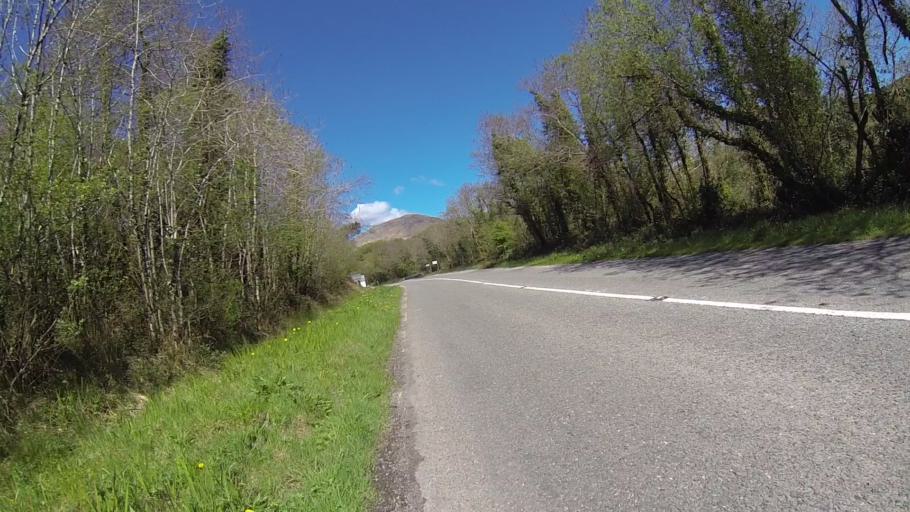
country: IE
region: Munster
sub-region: Ciarrai
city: Kenmare
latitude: 51.9012
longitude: -9.5986
